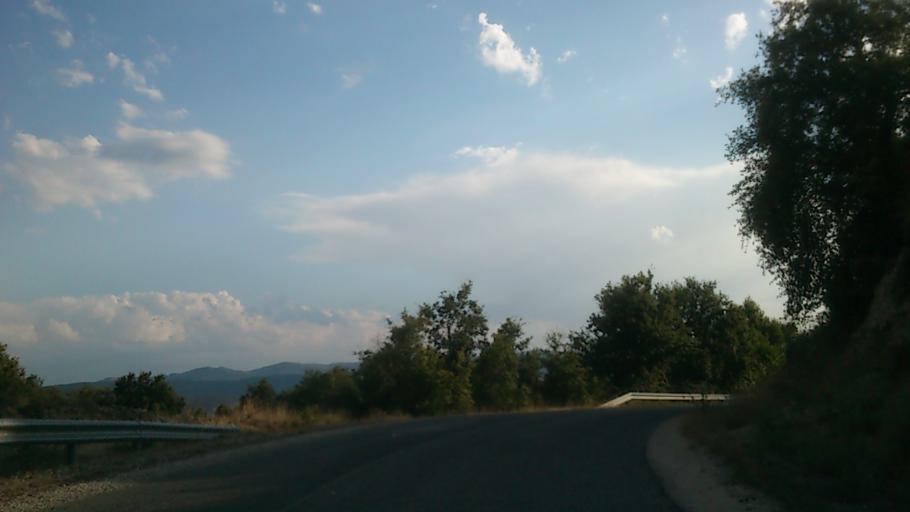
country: ES
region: Castille and Leon
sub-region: Provincia de Burgos
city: Frias
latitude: 42.8123
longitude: -3.2490
